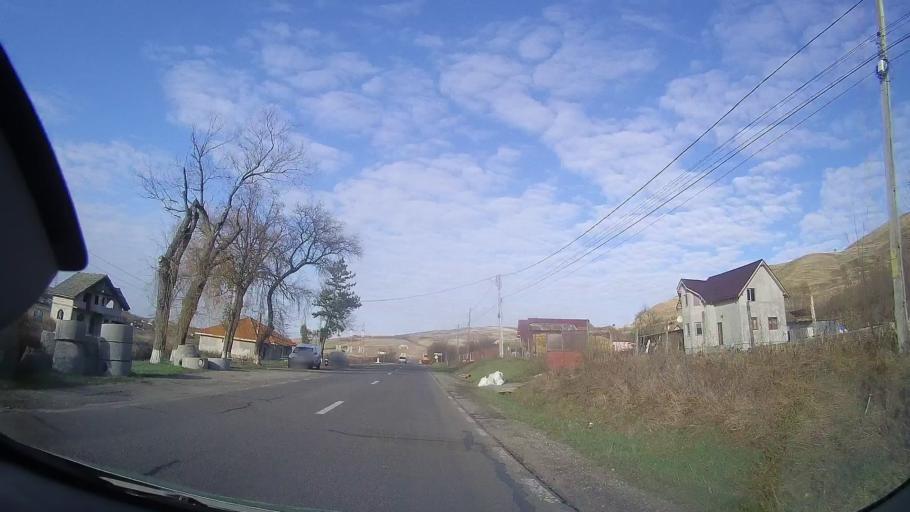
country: RO
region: Cluj
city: Caianu Mic
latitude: 46.8064
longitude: 23.8733
